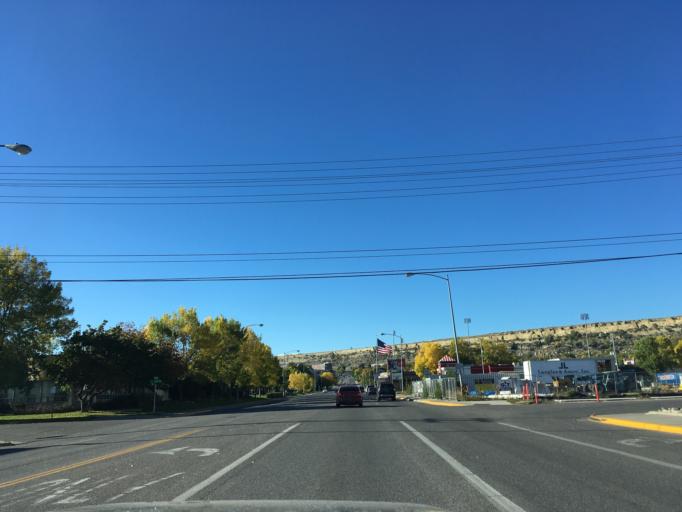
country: US
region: Montana
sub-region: Yellowstone County
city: Billings
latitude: 45.7875
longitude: -108.5093
